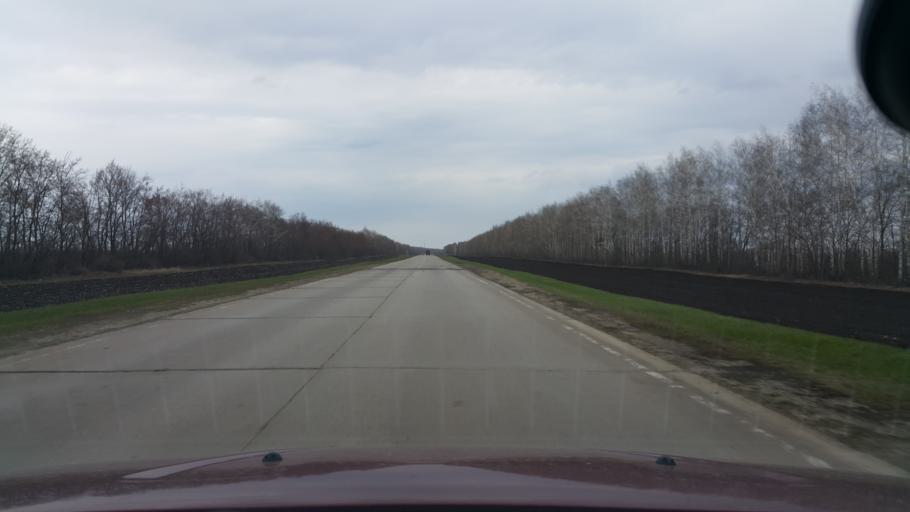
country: RU
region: Tambov
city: Bokino
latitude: 52.5647
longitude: 41.3666
